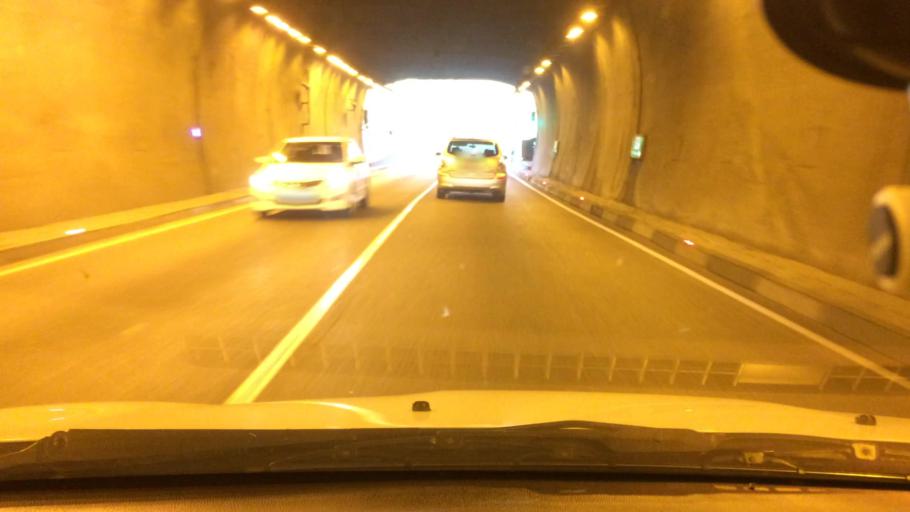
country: GE
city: Surami
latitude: 42.0619
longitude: 43.4916
